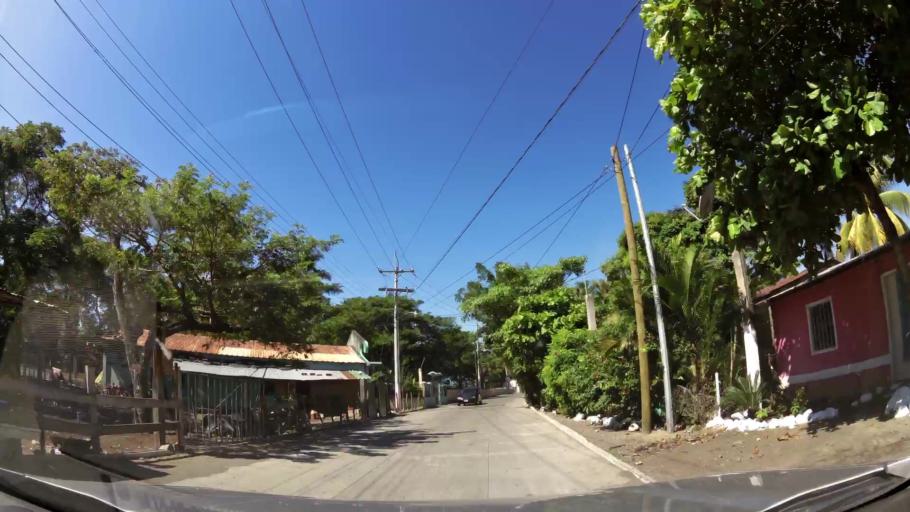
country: GT
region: Escuintla
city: Iztapa
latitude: 13.9389
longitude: -90.7077
